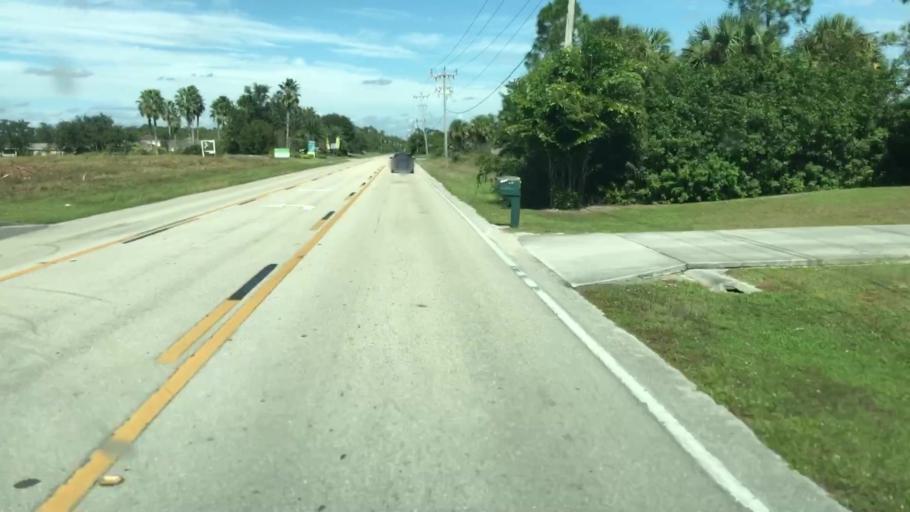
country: US
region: Florida
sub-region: Lee County
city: Lehigh Acres
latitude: 26.6230
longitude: -81.6462
